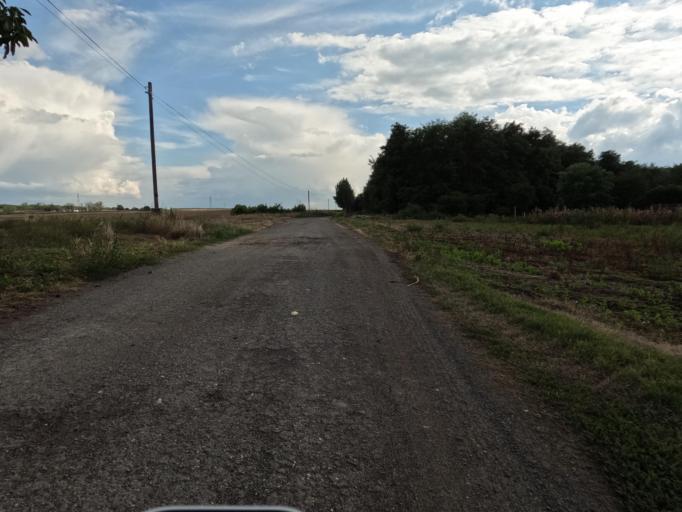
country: HU
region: Tolna
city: Tengelic
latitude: 46.5230
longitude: 18.7042
